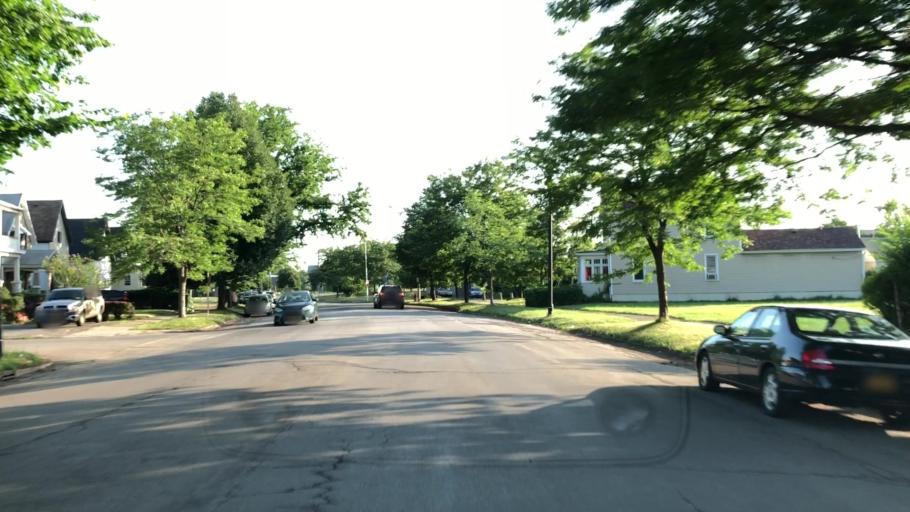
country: US
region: New York
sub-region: Erie County
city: Buffalo
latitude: 42.8757
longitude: -78.8433
